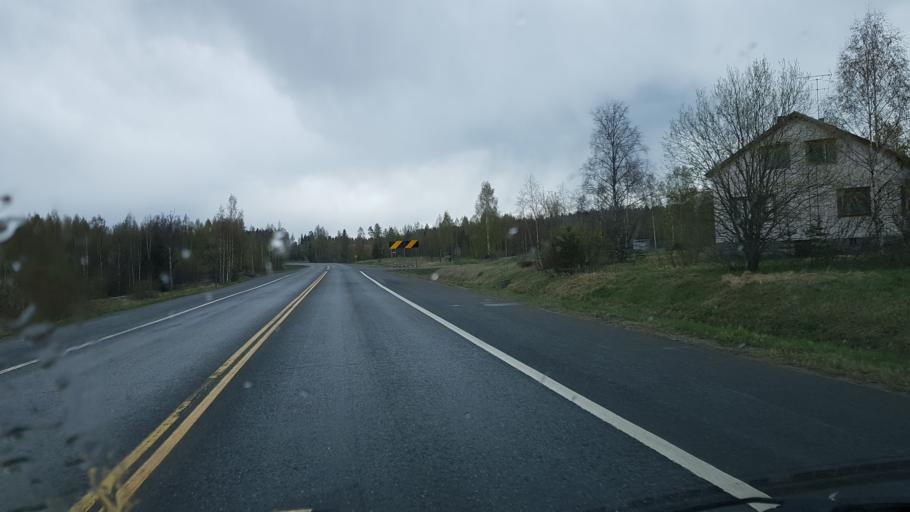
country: FI
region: Pirkanmaa
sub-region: Tampere
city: Pirkkala
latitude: 61.4223
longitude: 23.6346
